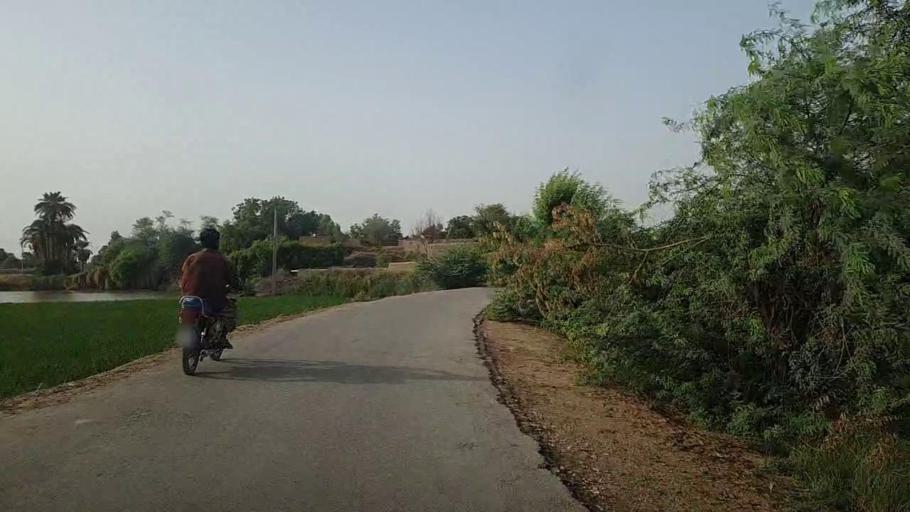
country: PK
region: Sindh
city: Mehar
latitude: 27.1333
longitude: 67.7913
